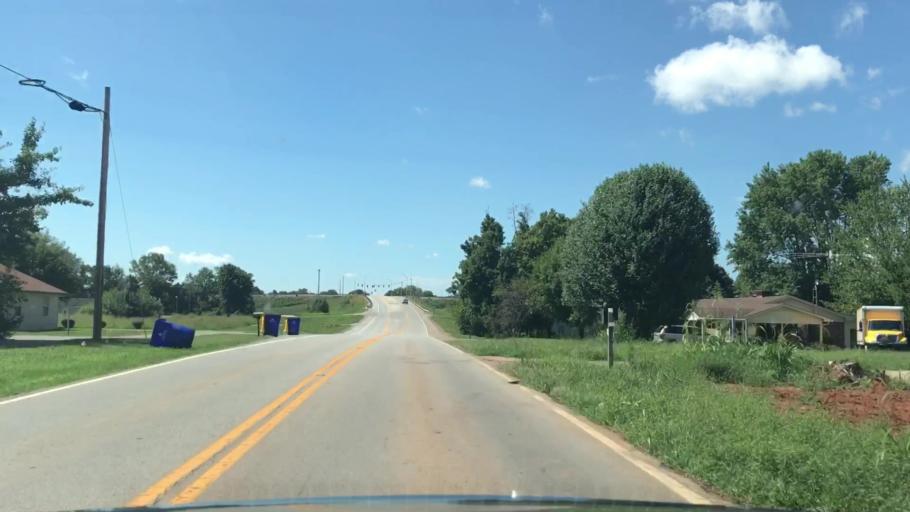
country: US
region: Kentucky
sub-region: Warren County
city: Plano
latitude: 36.9115
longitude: -86.4153
